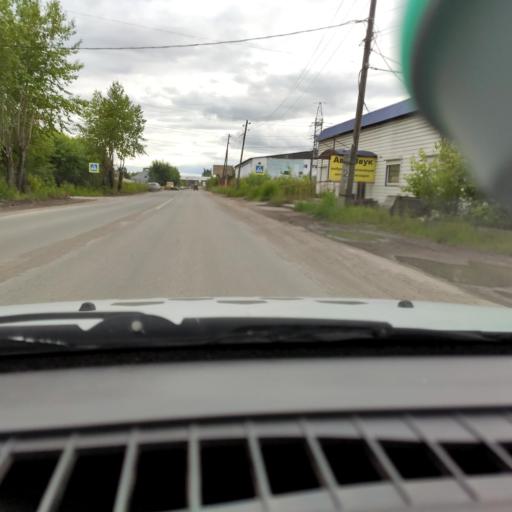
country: RU
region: Perm
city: Chusovoy
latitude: 58.2988
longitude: 57.8140
